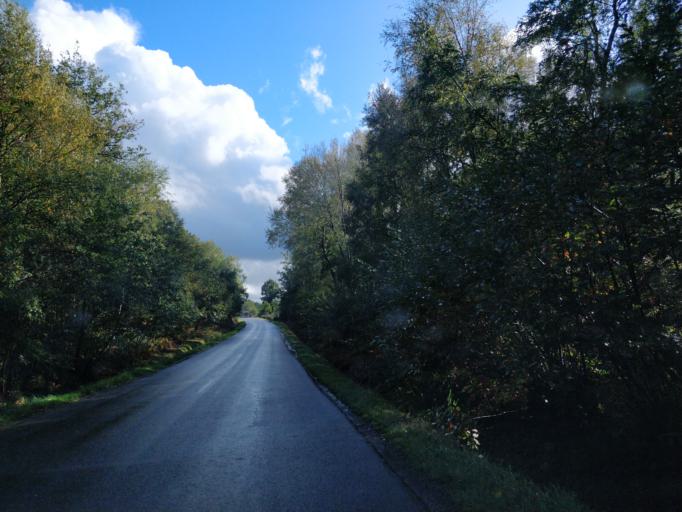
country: FR
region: Brittany
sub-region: Departement d'Ille-et-Vilaine
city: Chateaubourg
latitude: 48.1476
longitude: -1.4048
